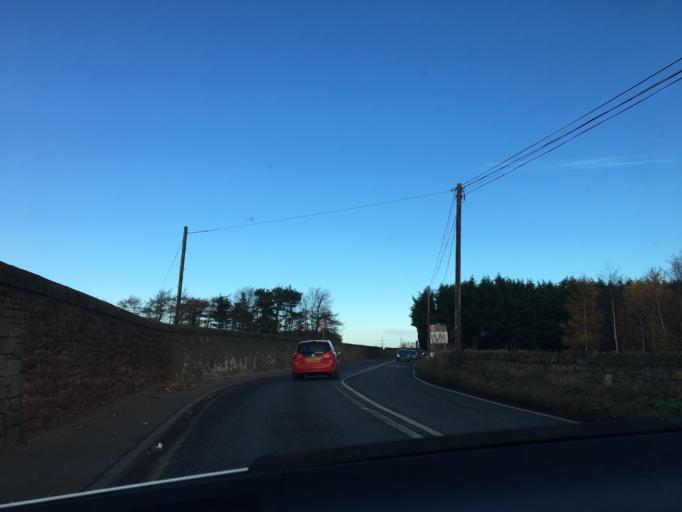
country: GB
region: Scotland
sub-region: Midlothian
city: Dalkeith
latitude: 55.8998
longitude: -3.0530
